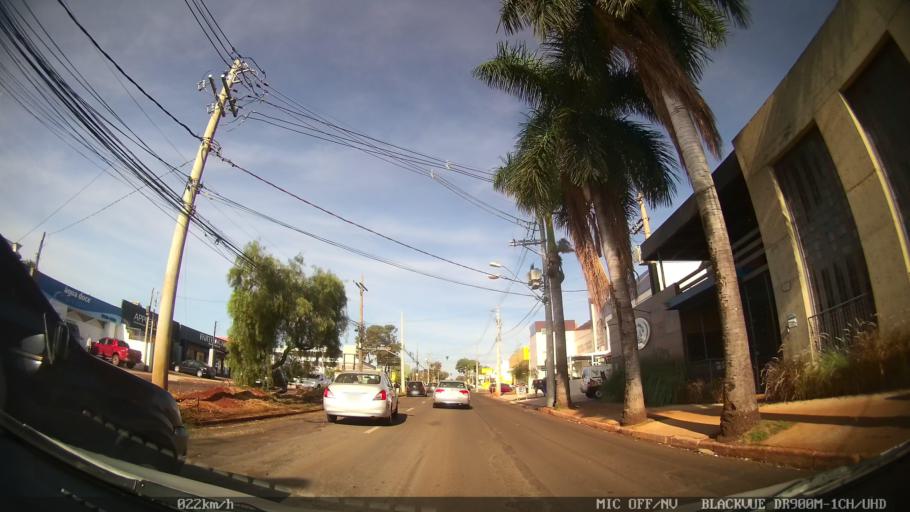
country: BR
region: Sao Paulo
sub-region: Ribeirao Preto
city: Ribeirao Preto
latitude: -21.1902
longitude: -47.8090
